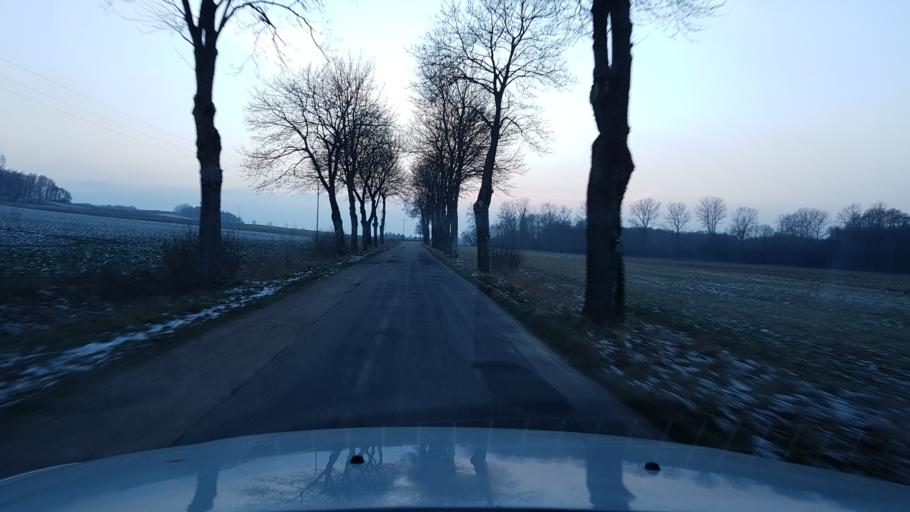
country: PL
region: West Pomeranian Voivodeship
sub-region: Powiat bialogardzki
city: Karlino
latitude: 53.9907
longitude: 15.8160
